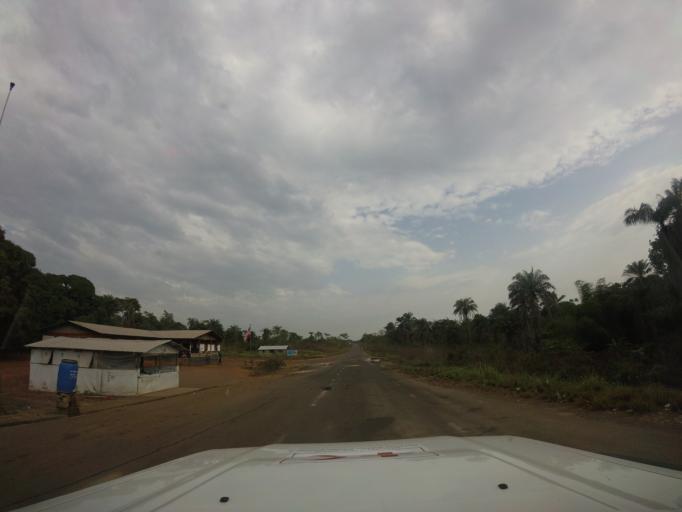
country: LR
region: Grand Cape Mount
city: Robertsport
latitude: 6.9655
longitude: -11.3113
